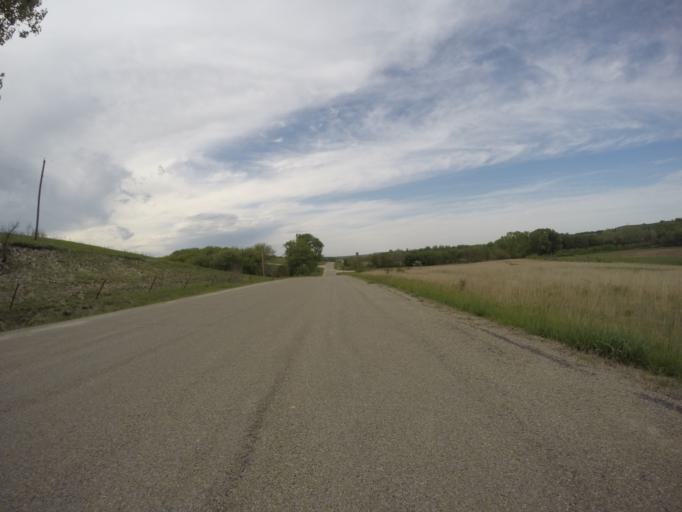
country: US
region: Kansas
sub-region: Riley County
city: Ogden
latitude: 39.0050
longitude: -96.6018
